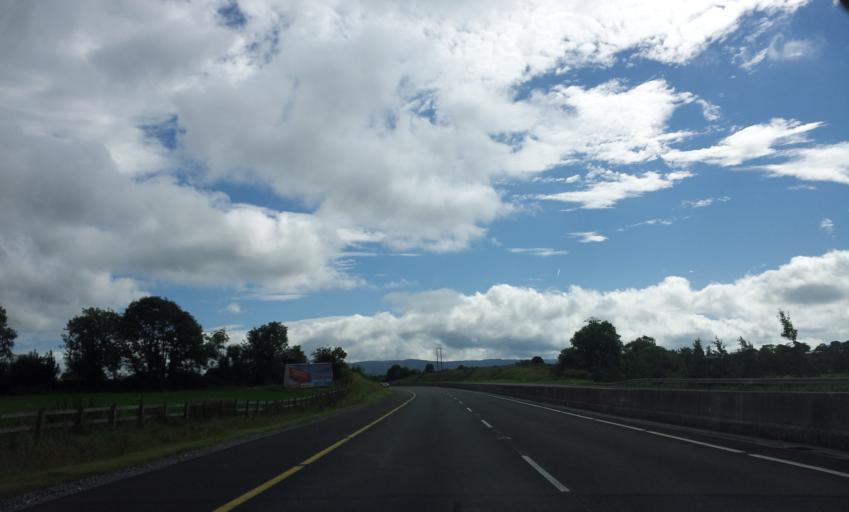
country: IE
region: Munster
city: Nenagh Bridge
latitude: 52.8689
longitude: -8.0719
